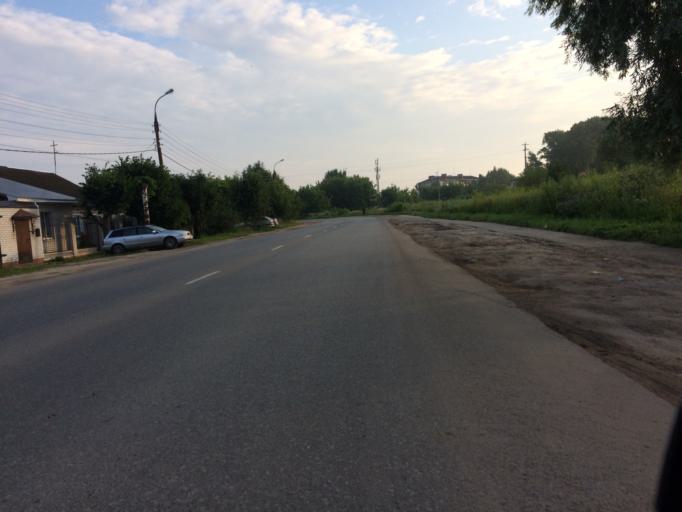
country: RU
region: Mariy-El
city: Yoshkar-Ola
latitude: 56.6465
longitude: 47.9545
